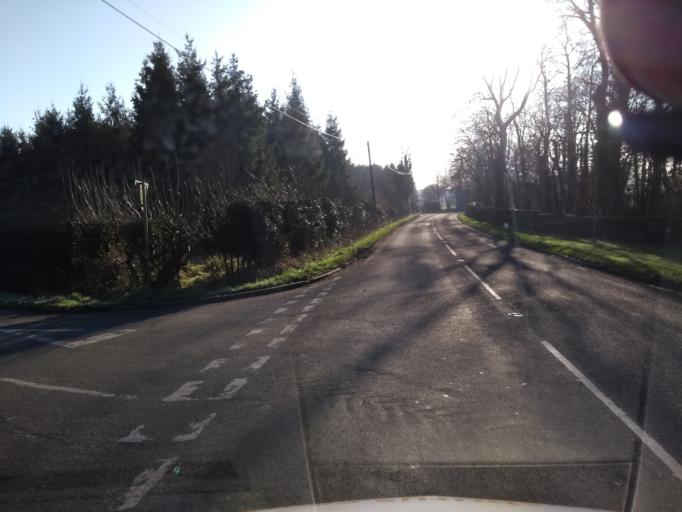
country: GB
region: England
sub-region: Somerset
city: Redlynch
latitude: 51.0992
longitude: -2.4264
